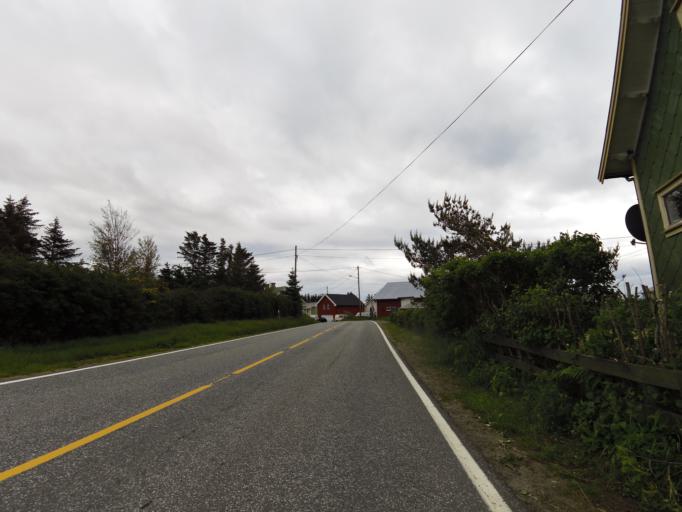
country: NO
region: Vest-Agder
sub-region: Farsund
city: Vestbygd
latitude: 58.1198
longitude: 6.6002
